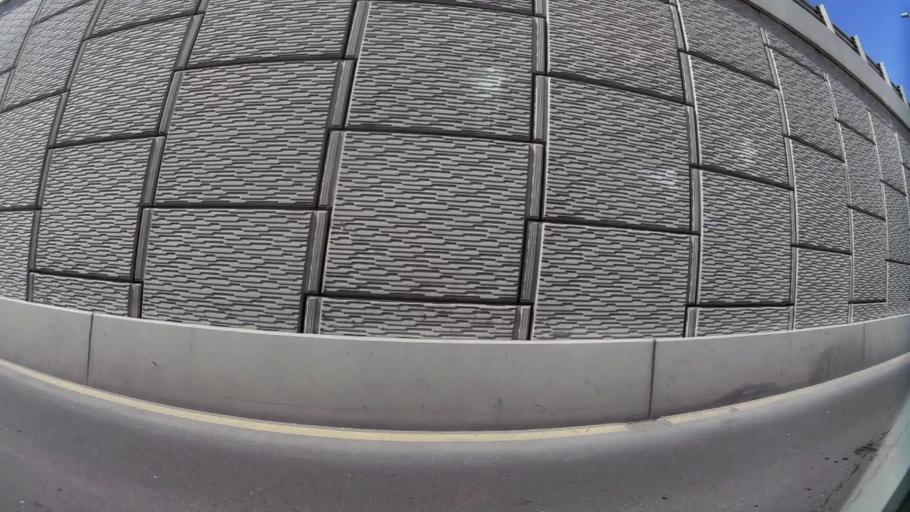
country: BH
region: Manama
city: Manama
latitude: 26.2044
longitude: 50.6015
